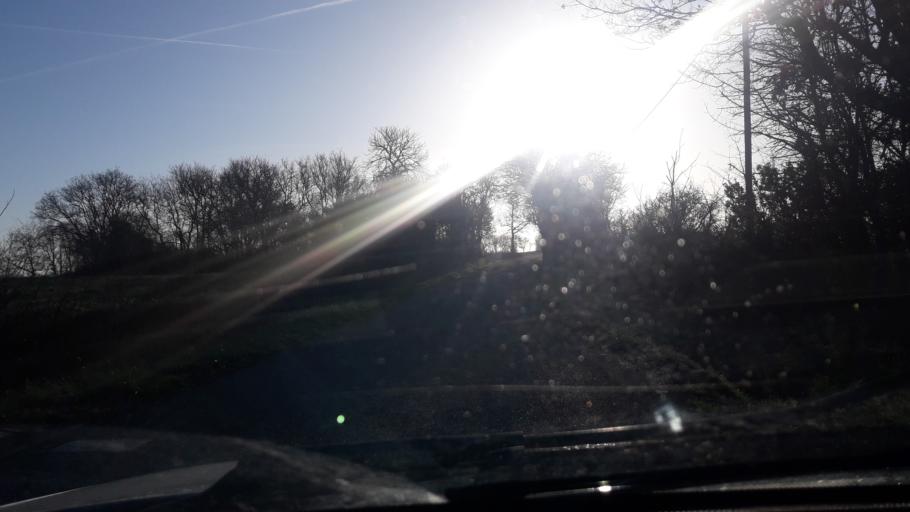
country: FR
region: Midi-Pyrenees
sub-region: Departement du Gers
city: Gimont
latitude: 43.6500
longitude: 0.9892
